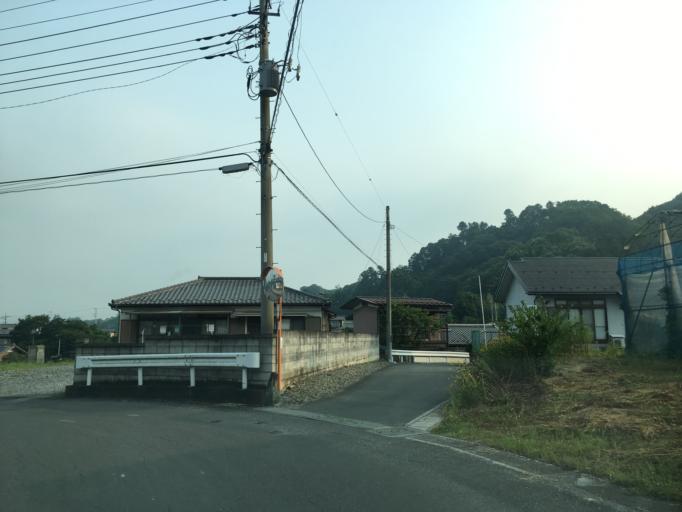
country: JP
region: Saitama
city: Chichibu
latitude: 35.9817
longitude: 139.1129
